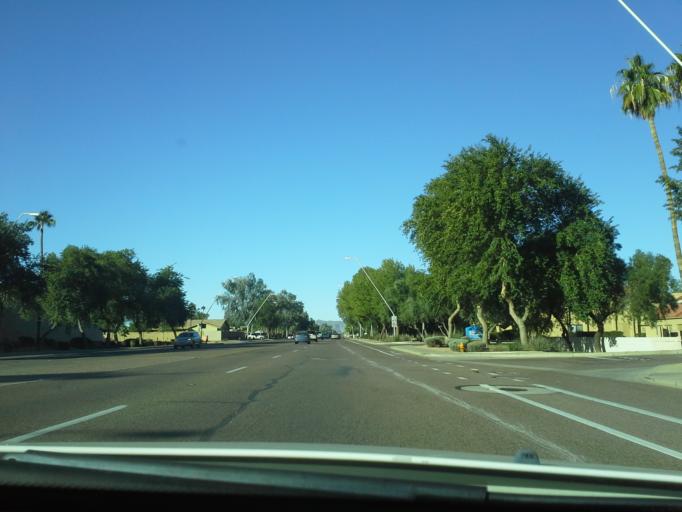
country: US
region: Arizona
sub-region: Maricopa County
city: San Carlos
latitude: 33.3498
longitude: -111.8604
